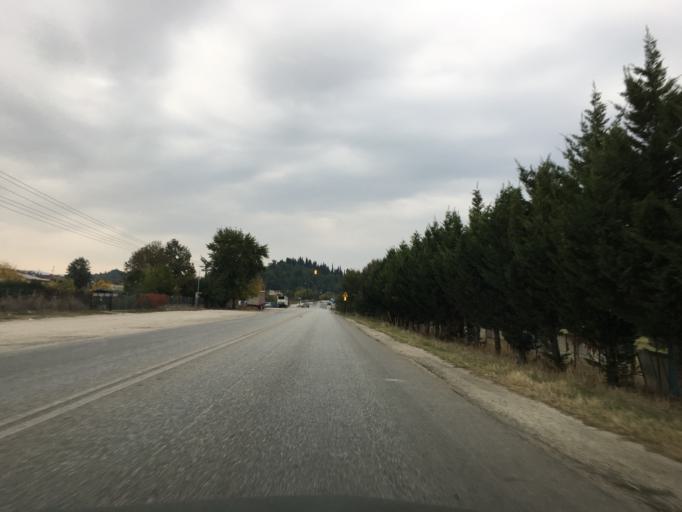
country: GR
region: Thessaly
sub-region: Trikala
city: Trikala
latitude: 39.5703
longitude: 21.7584
